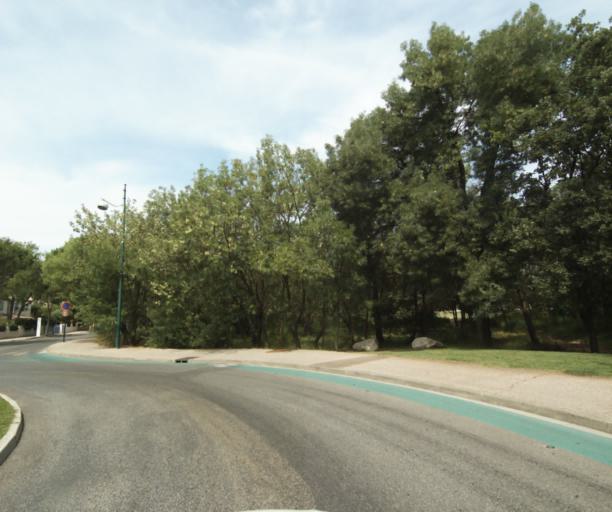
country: FR
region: Provence-Alpes-Cote d'Azur
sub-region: Departement du Var
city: La Garde
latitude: 43.1310
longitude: 6.0230
